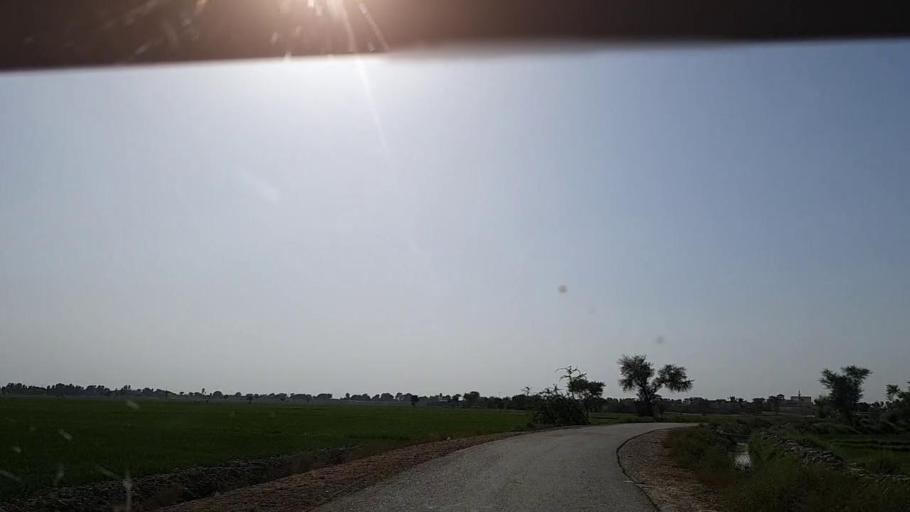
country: PK
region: Sindh
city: Phulji
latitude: 26.9889
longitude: 67.6550
